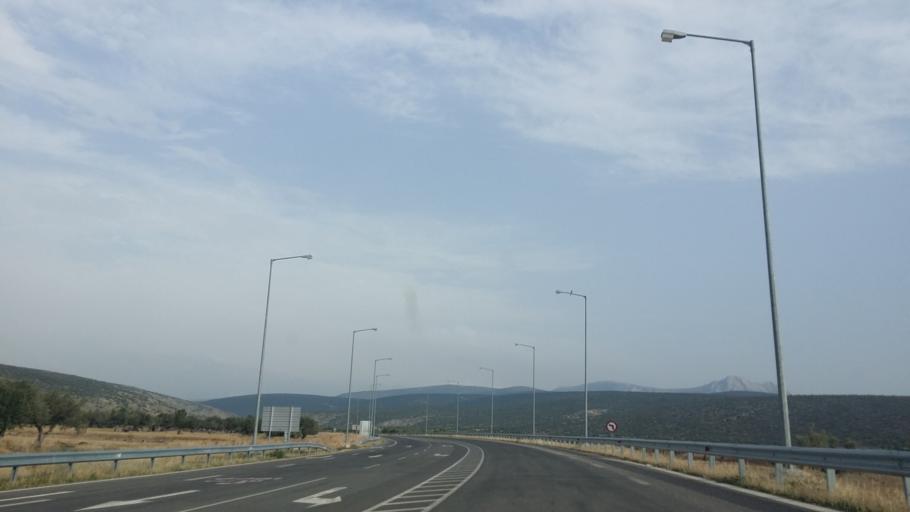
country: GR
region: Central Greece
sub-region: Nomos Voiotias
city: Korini
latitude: 38.2455
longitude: 22.9792
